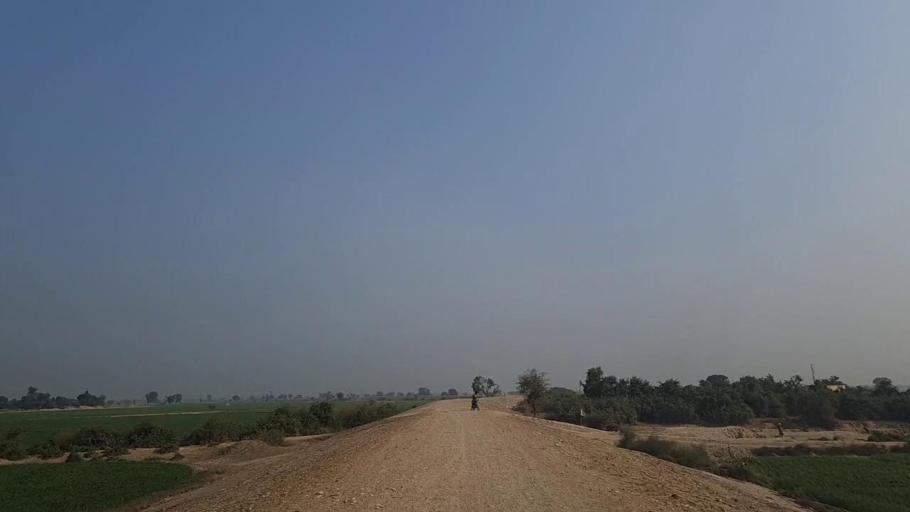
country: PK
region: Sindh
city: Sann
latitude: 26.0890
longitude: 68.1543
